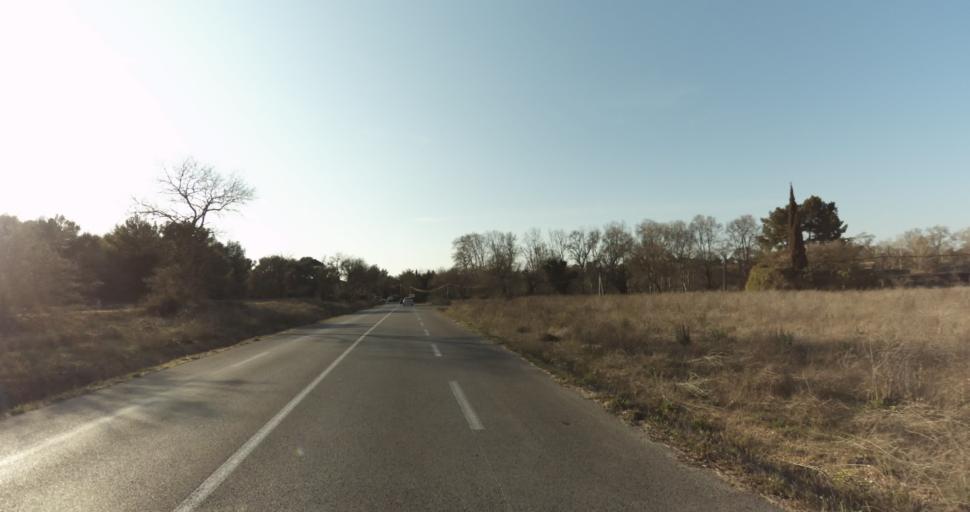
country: FR
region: Provence-Alpes-Cote d'Azur
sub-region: Departement des Bouches-du-Rhone
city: Ventabren
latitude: 43.5022
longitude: 5.3469
